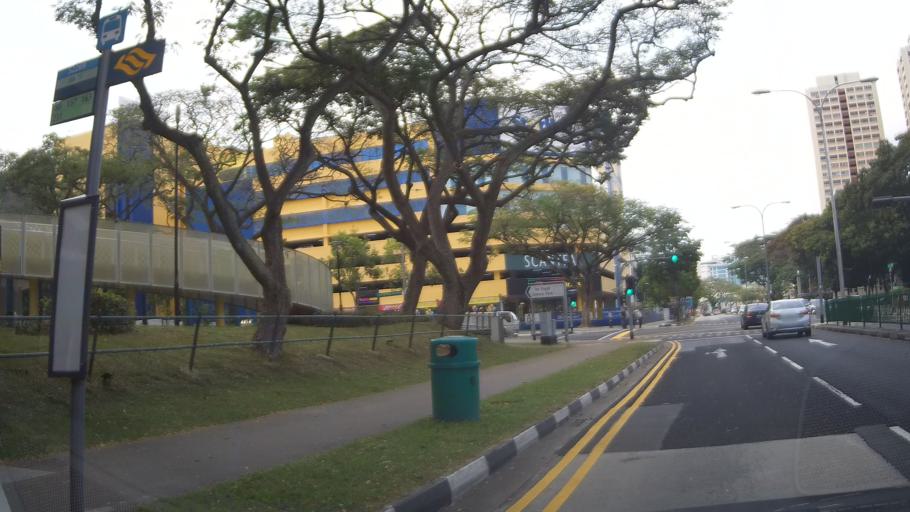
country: SG
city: Singapore
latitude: 1.3340
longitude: 103.8514
